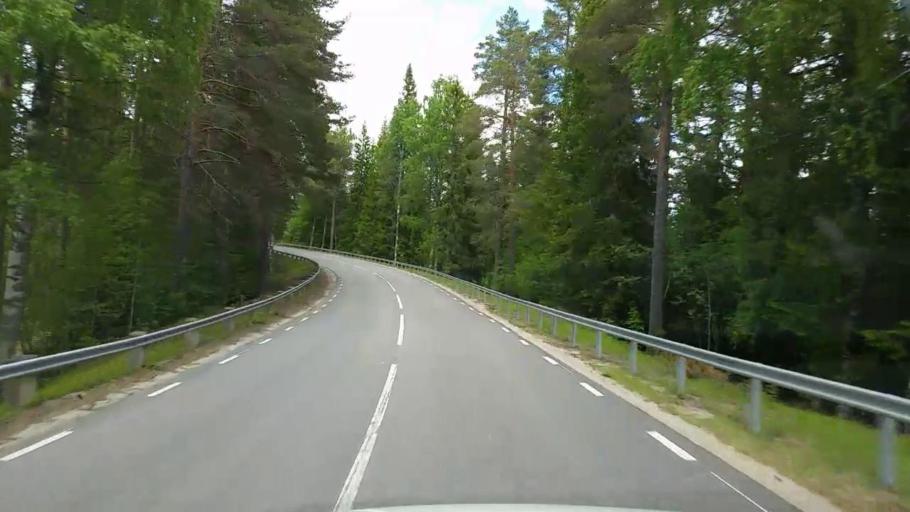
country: SE
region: Gaevleborg
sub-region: Bollnas Kommun
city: Vittsjo
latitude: 61.1412
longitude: 16.1694
